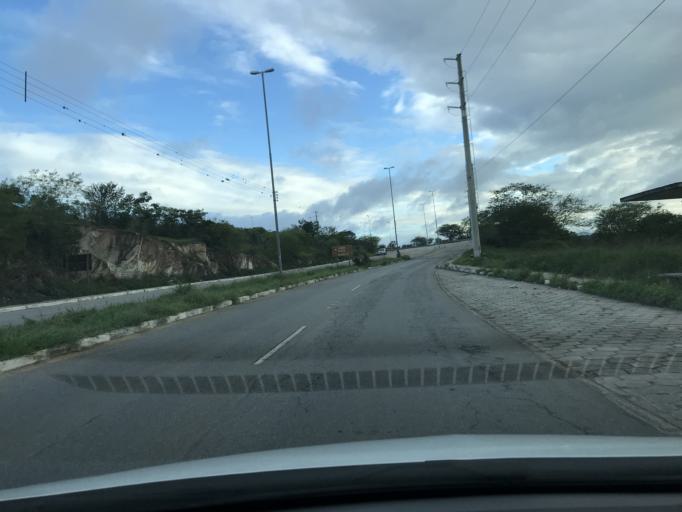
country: BR
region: Pernambuco
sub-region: Caruaru
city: Caruaru
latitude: -8.3044
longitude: -35.9410
